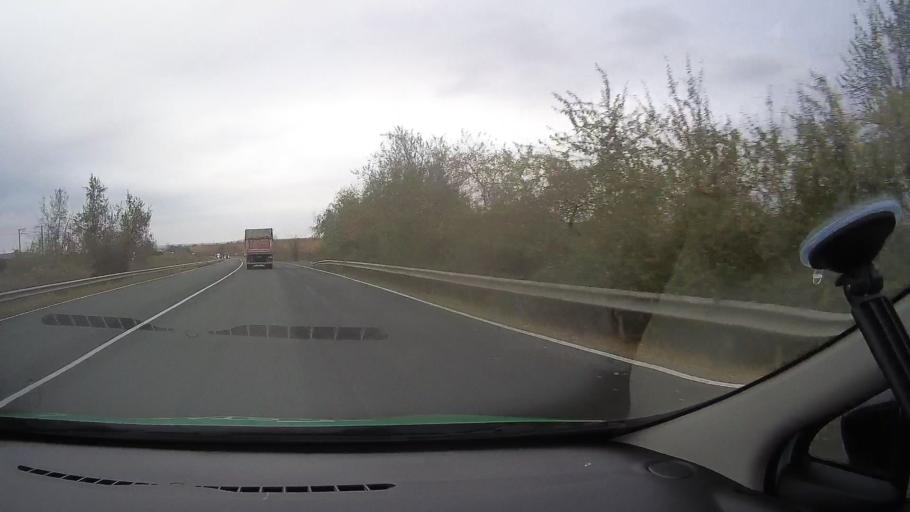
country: RO
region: Constanta
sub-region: Comuna Poarta Alba
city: Poarta Alba
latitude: 44.2195
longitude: 28.3884
